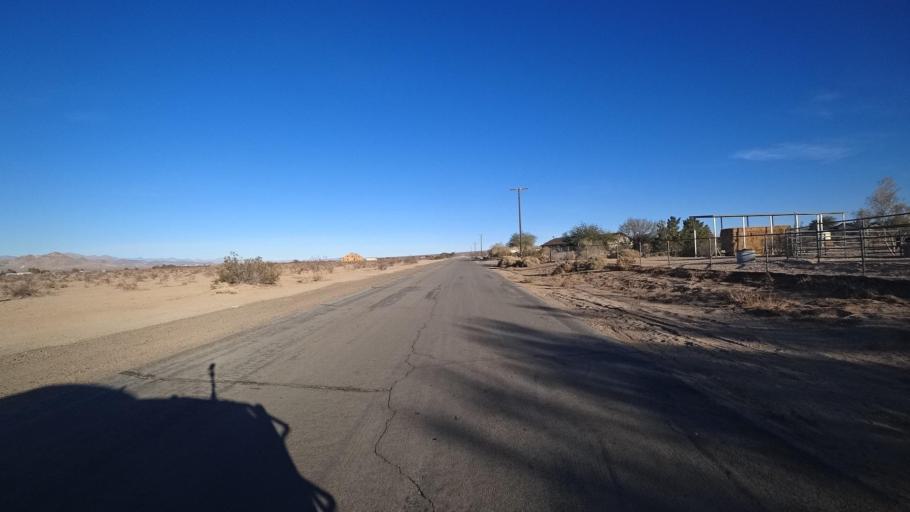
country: US
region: California
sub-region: Kern County
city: Ridgecrest
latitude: 35.6006
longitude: -117.6520
